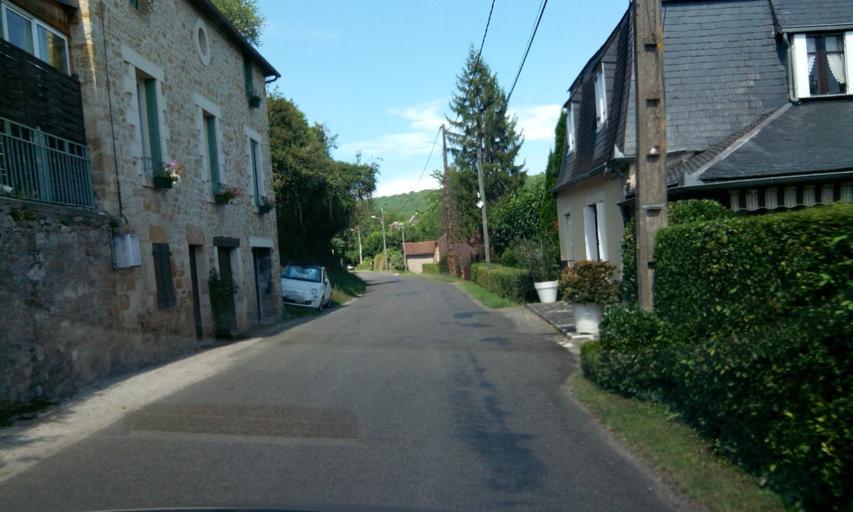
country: FR
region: Midi-Pyrenees
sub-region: Departement du Lot
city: Vayrac
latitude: 44.9371
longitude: 1.6592
